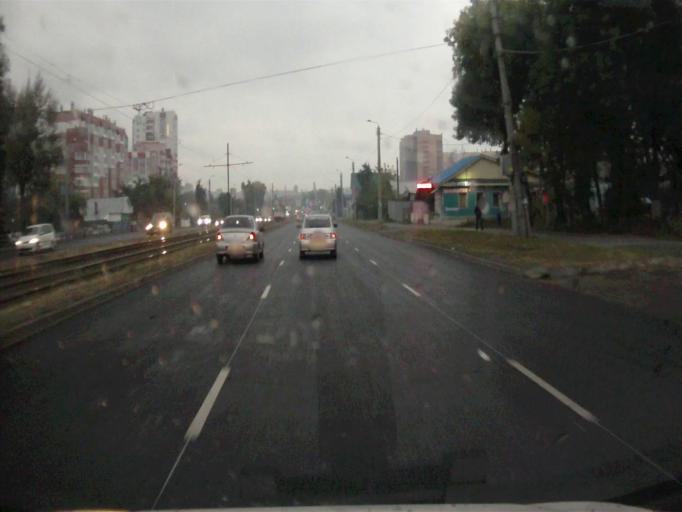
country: RU
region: Chelyabinsk
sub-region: Gorod Chelyabinsk
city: Chelyabinsk
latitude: 55.1838
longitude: 61.3794
